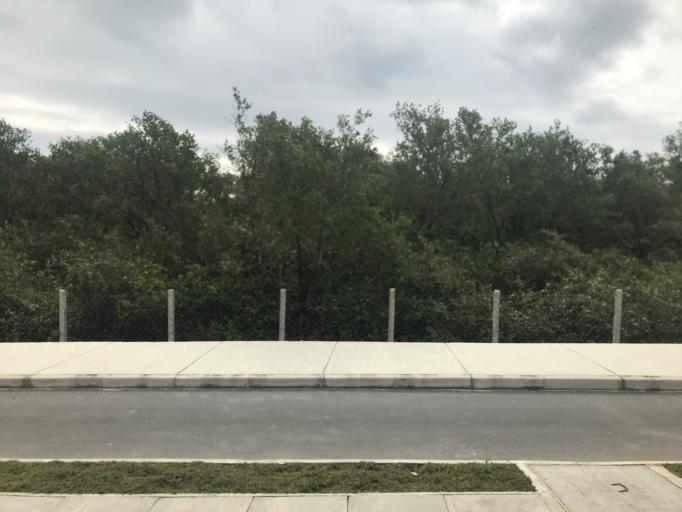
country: BR
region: Santa Catarina
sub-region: Florianopolis
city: Costeira do Pirajubae
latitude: -27.6537
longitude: -48.5242
